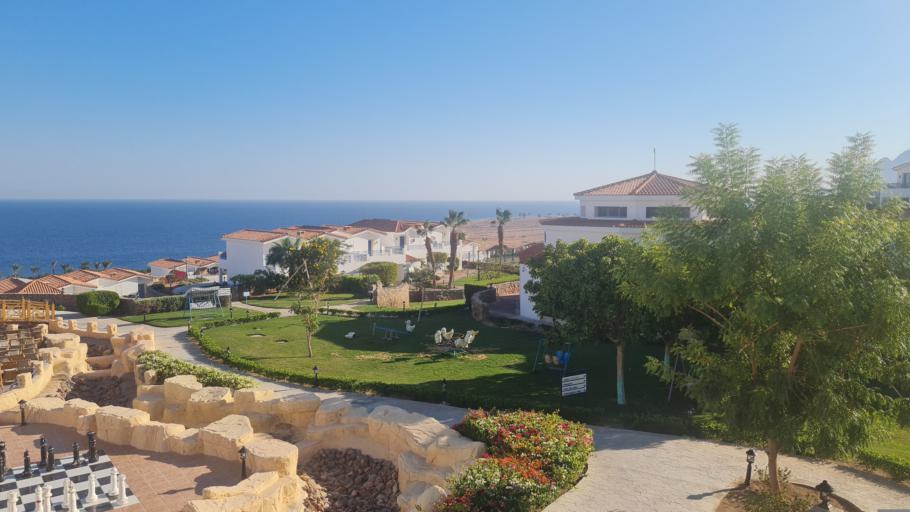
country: EG
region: South Sinai
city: Dhahab
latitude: 28.4594
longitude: 34.4682
